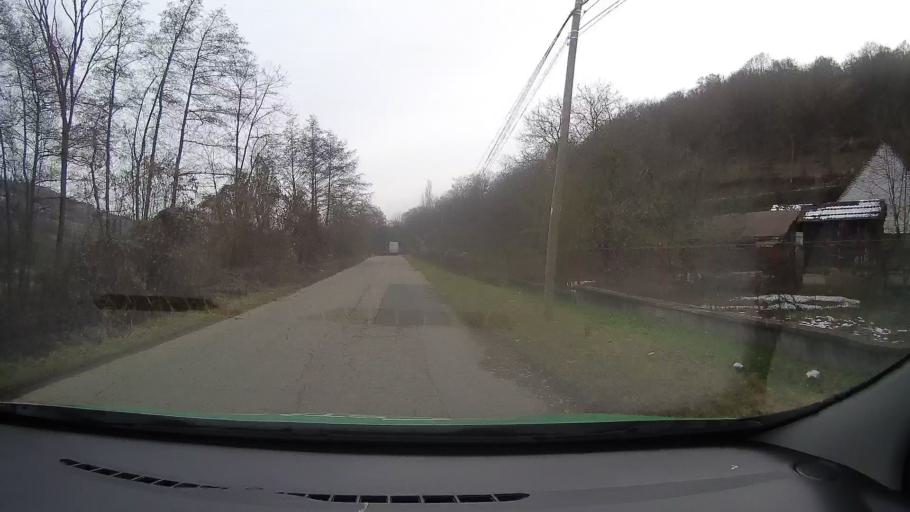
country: RO
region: Hunedoara
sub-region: Comuna Geoagiu
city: Geoagiu
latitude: 45.9398
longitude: 23.1819
